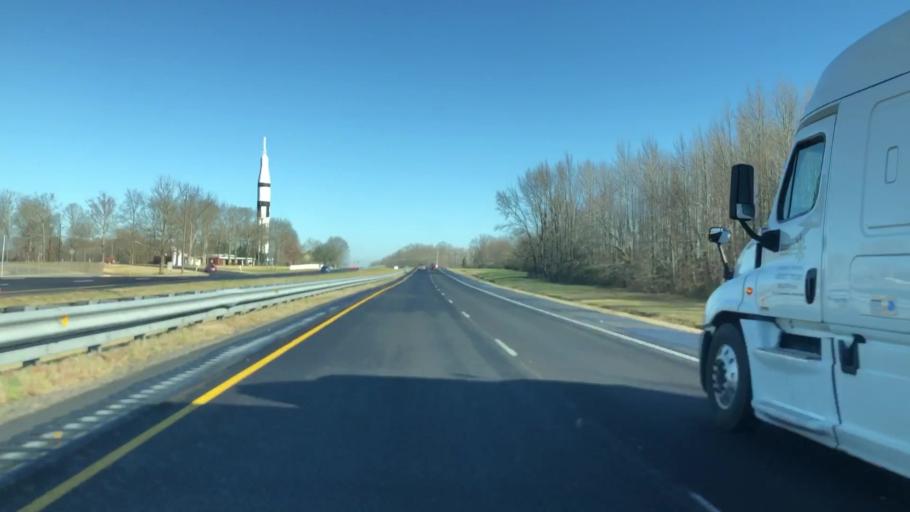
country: US
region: Alabama
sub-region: Limestone County
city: Ardmore
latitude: 34.9506
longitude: -86.8930
